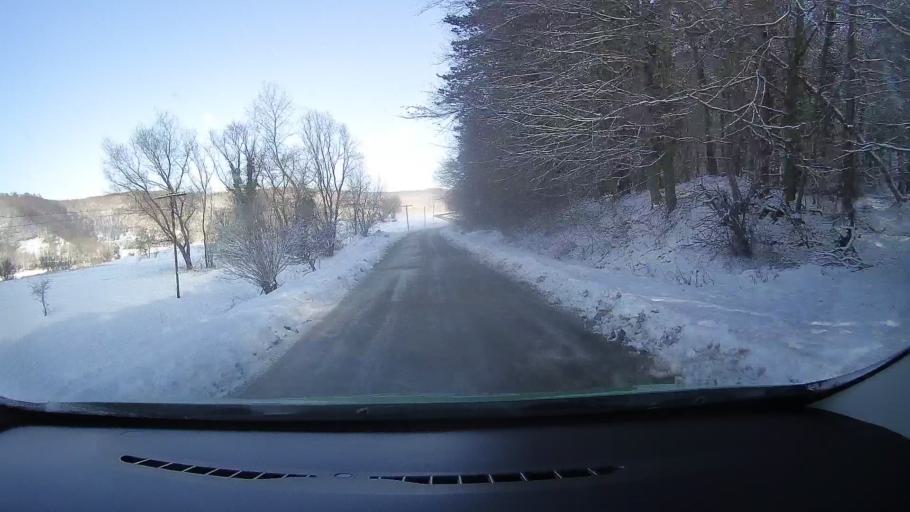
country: RO
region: Sibiu
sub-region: Comuna Mosna
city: Mosna
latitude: 46.0186
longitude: 24.4120
